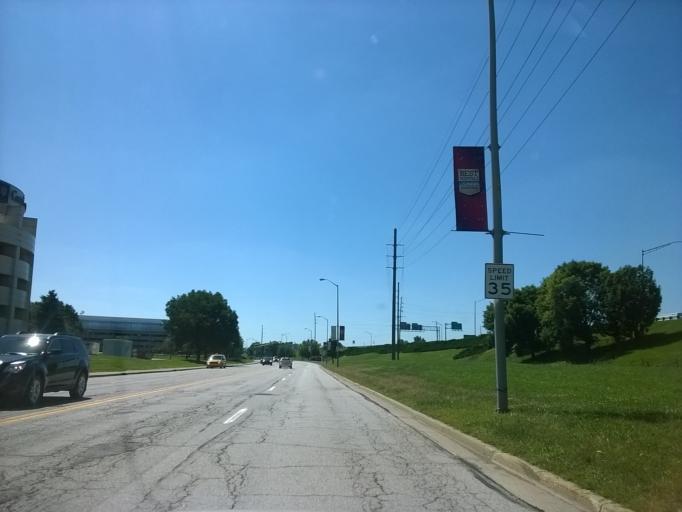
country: US
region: Indiana
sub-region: Marion County
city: Indianapolis
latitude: 39.7923
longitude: -86.1644
